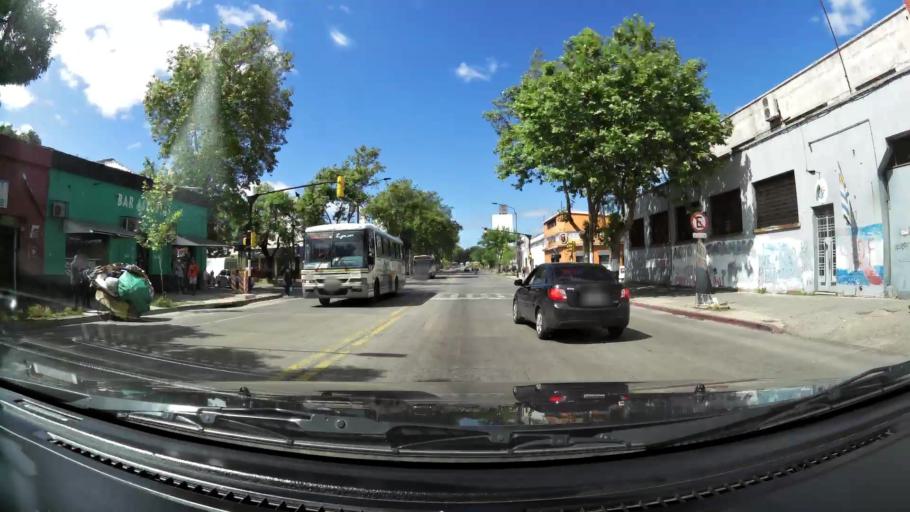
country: UY
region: Montevideo
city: Montevideo
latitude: -34.8614
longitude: -56.1338
